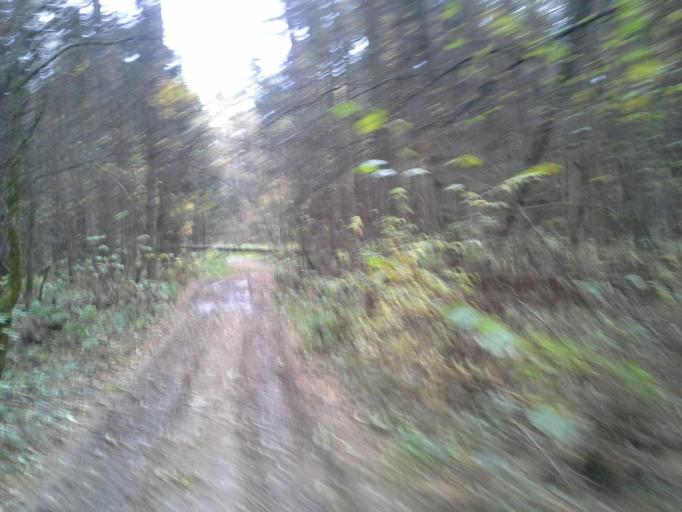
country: RU
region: Moskovskaya
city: Gorki Vtoryye
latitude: 55.6911
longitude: 37.1657
